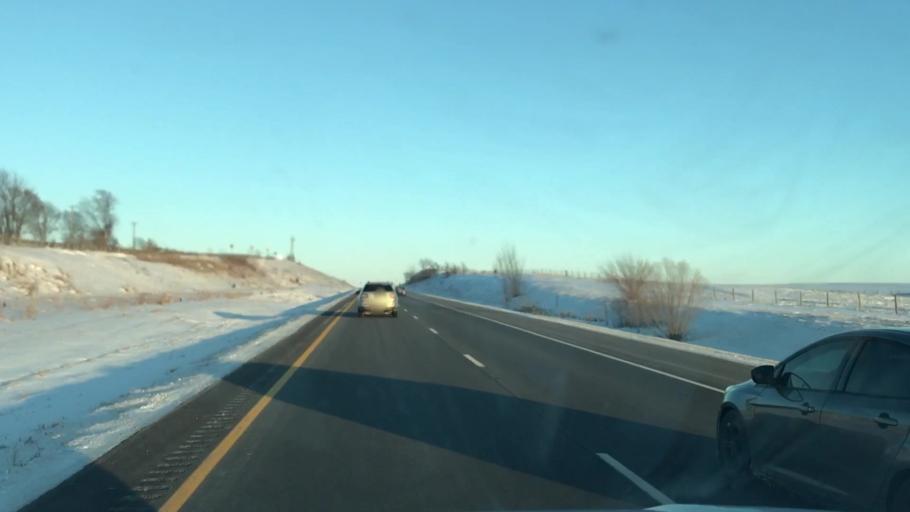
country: US
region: Missouri
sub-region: Clinton County
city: Gower
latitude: 39.7615
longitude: -94.5474
